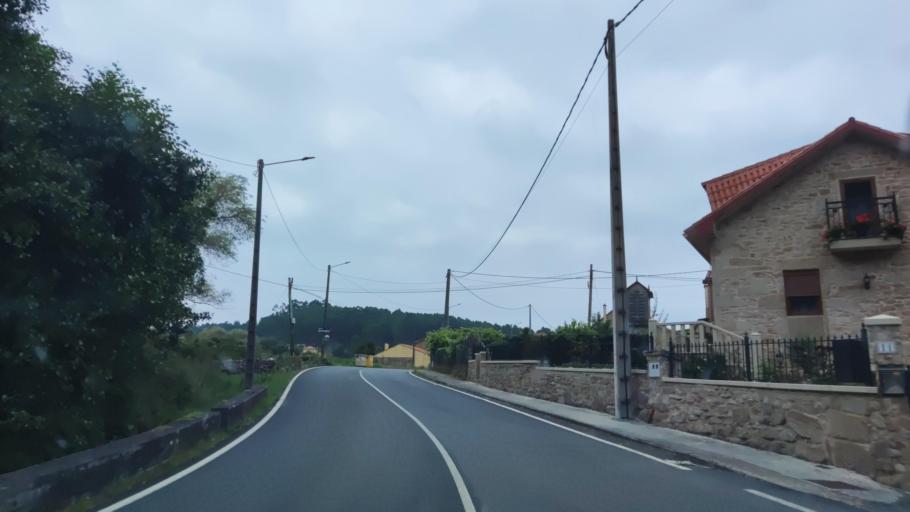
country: ES
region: Galicia
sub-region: Provincia de Pontevedra
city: Catoira
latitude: 42.6666
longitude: -8.7449
